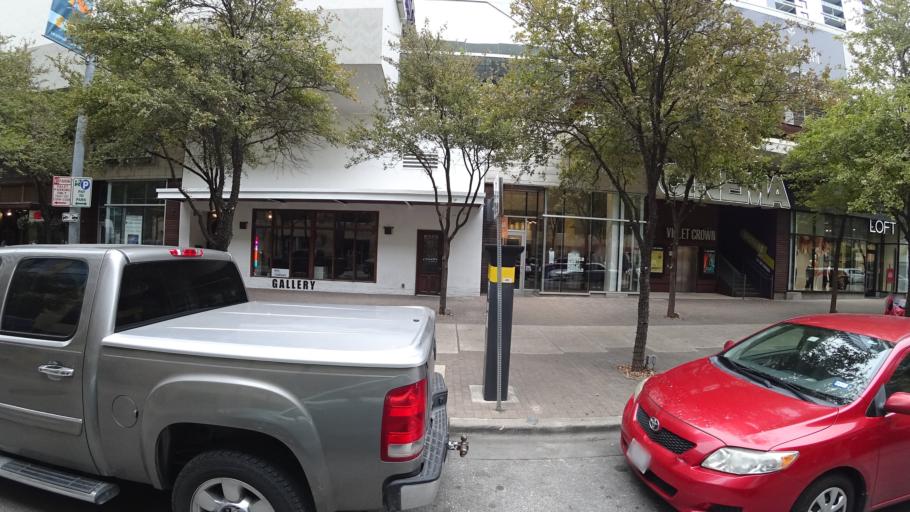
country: US
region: Texas
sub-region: Travis County
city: Austin
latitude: 30.2655
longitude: -97.7483
